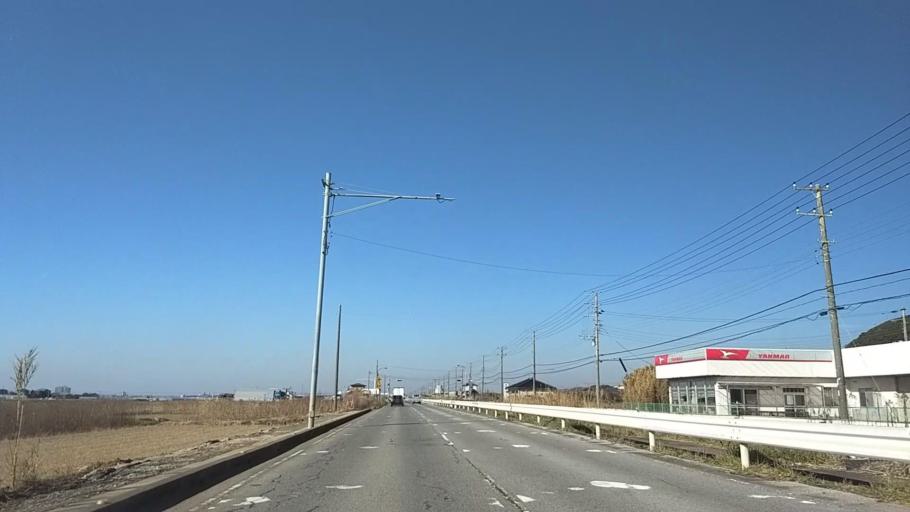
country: JP
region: Chiba
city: Asahi
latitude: 35.7142
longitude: 140.7091
